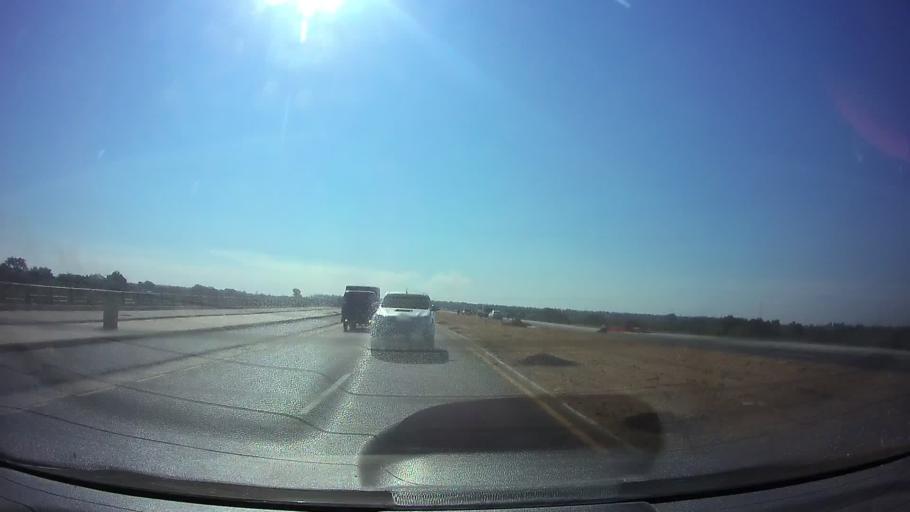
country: PY
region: Asuncion
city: Asuncion
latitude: -25.2606
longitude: -57.6071
